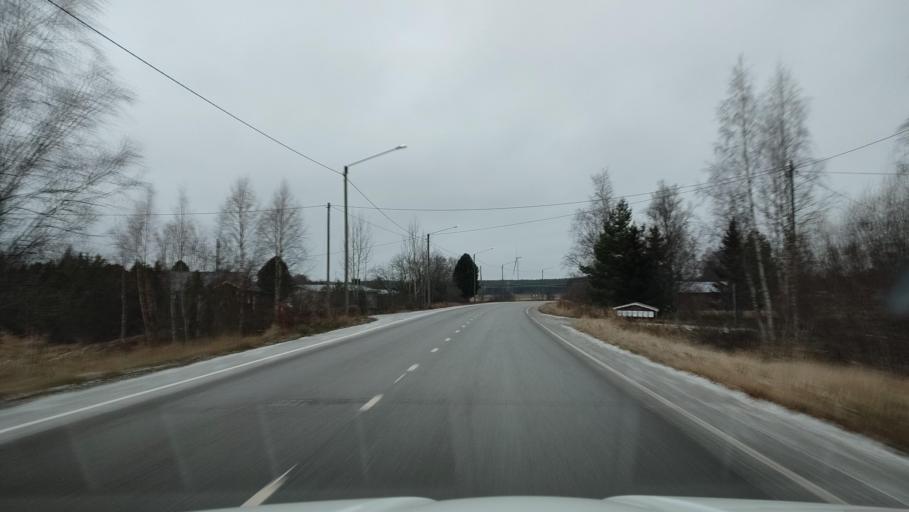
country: FI
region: Southern Ostrobothnia
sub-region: Suupohja
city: Karijoki
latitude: 62.2308
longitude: 21.6392
